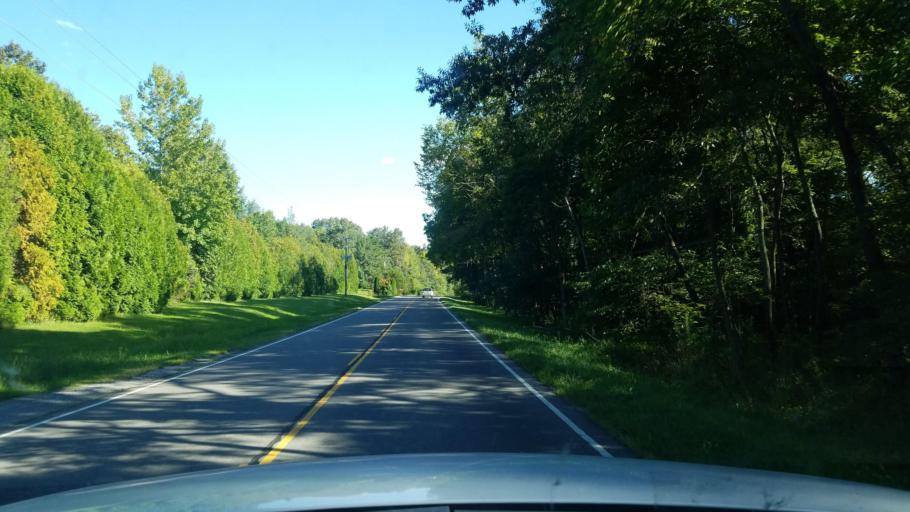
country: US
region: Illinois
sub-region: Saline County
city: Harrisburg
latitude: 37.6119
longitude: -88.4650
